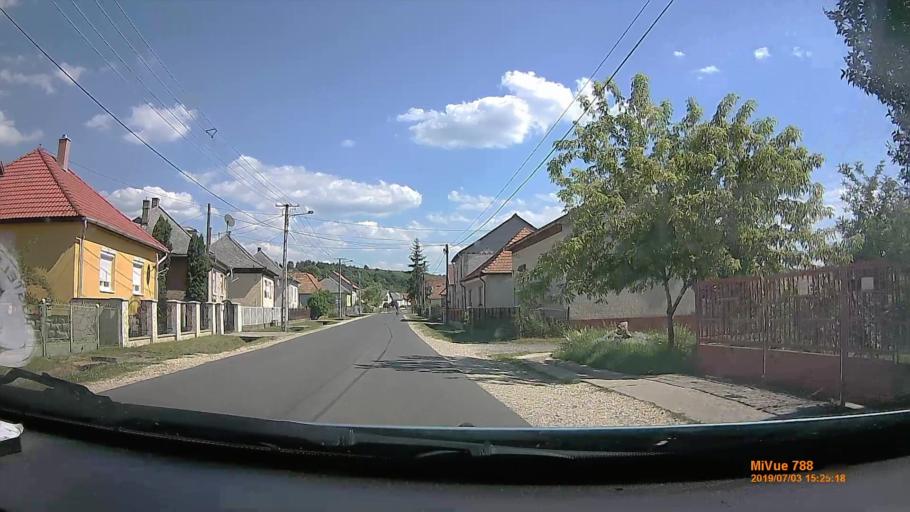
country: HU
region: Borsod-Abauj-Zemplen
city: Farkaslyuk
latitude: 48.1909
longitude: 20.3941
